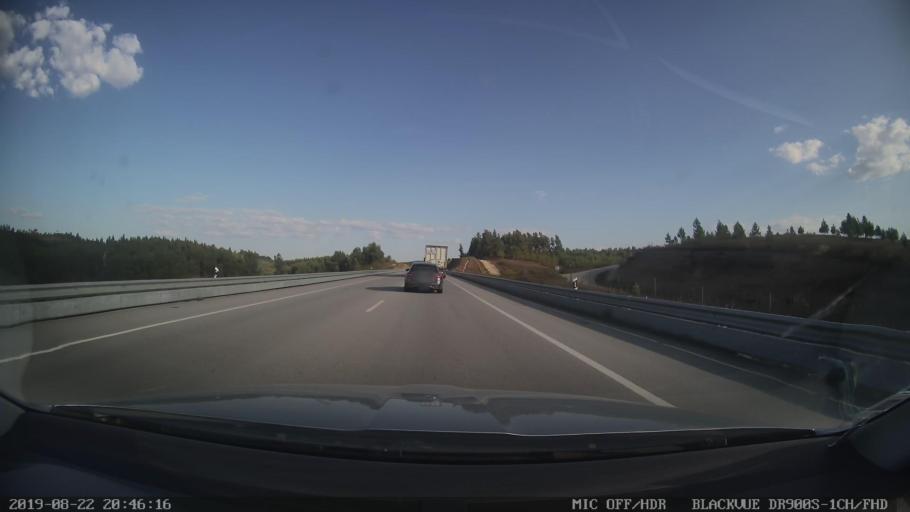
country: PT
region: Castelo Branco
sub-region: Proenca-A-Nova
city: Proenca-a-Nova
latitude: 39.7251
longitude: -7.8749
